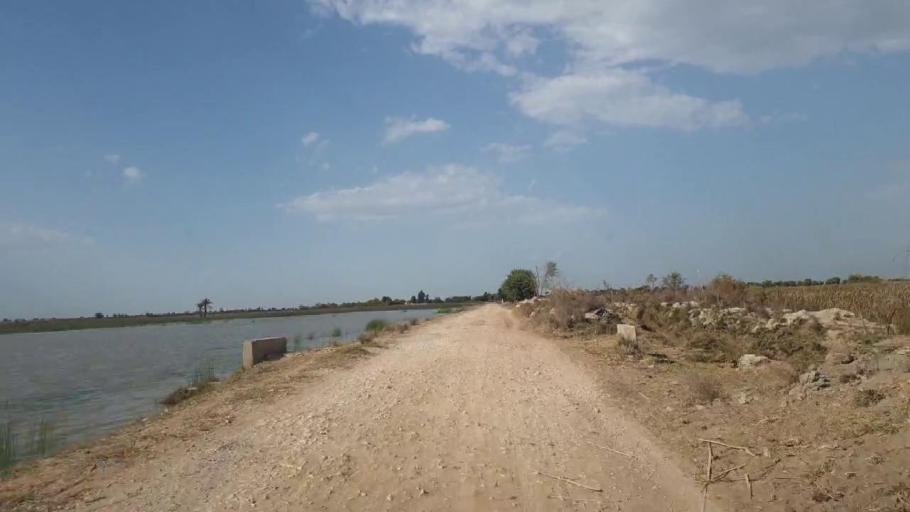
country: PK
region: Sindh
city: Shahdadpur
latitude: 25.9986
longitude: 68.4618
